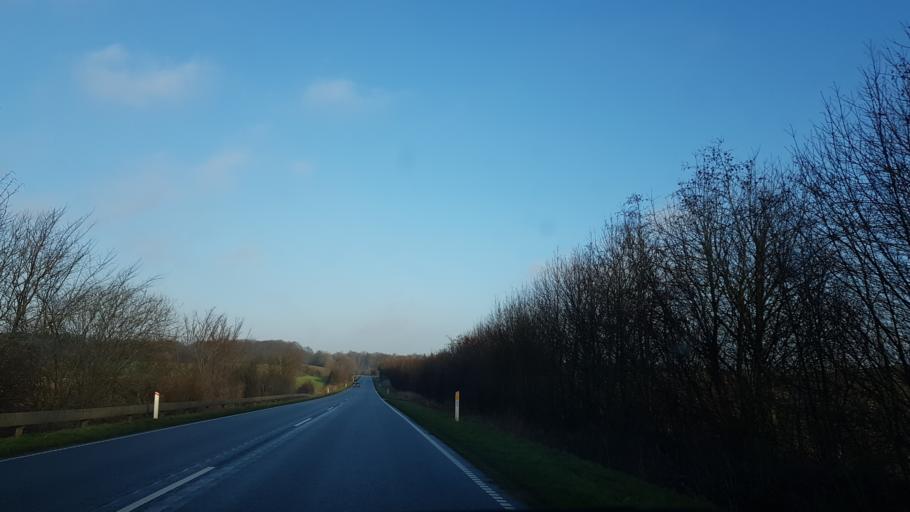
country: DK
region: South Denmark
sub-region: Haderslev Kommune
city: Haderslev
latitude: 55.1835
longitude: 9.4039
